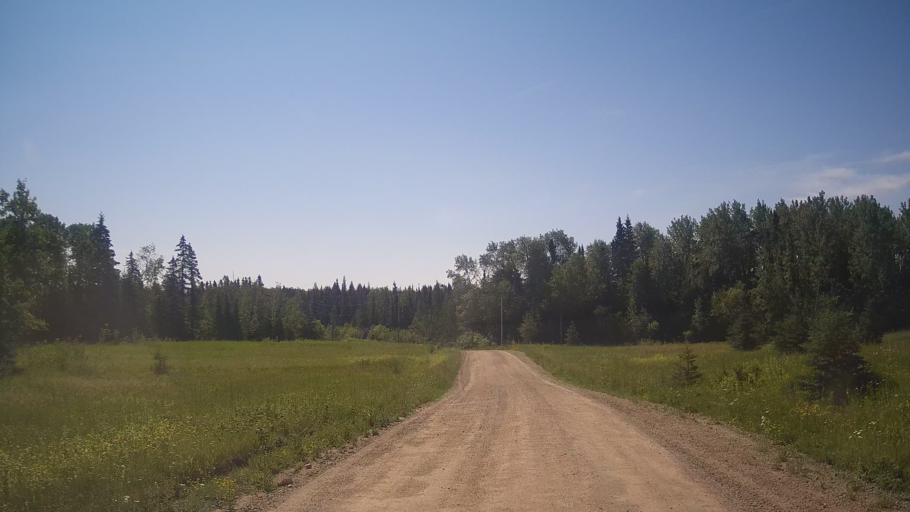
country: CA
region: Ontario
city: Dryden
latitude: 49.8202
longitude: -93.3373
